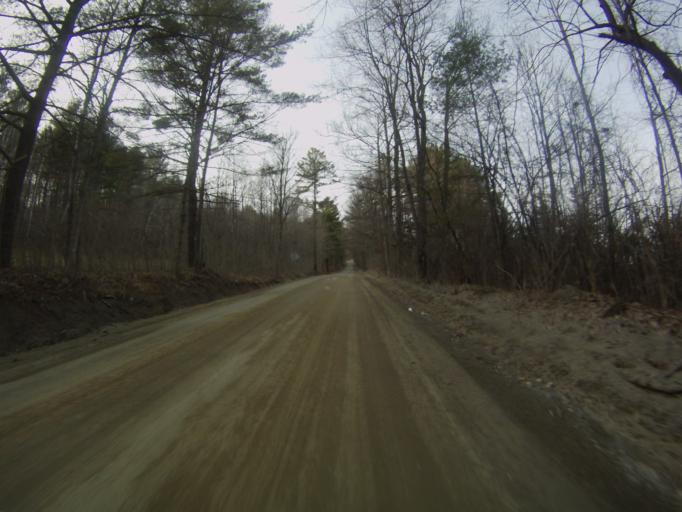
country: US
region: Vermont
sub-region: Addison County
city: Middlebury (village)
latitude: 44.0219
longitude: -73.2584
